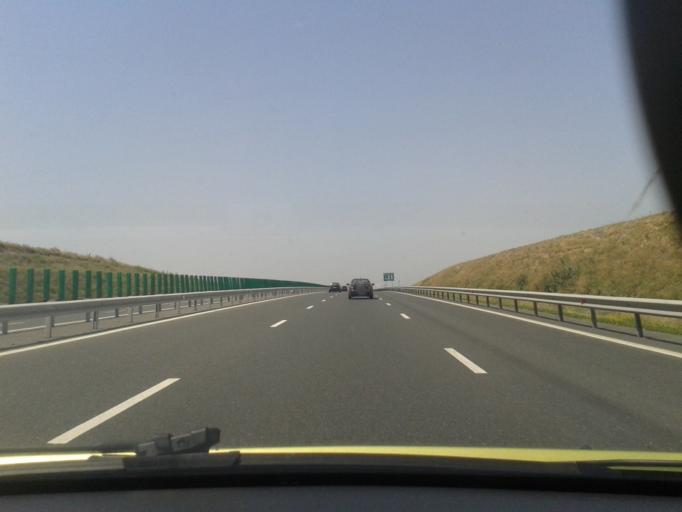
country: RO
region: Constanta
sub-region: Comuna Saligny
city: Saligny
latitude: 44.2710
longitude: 28.0597
